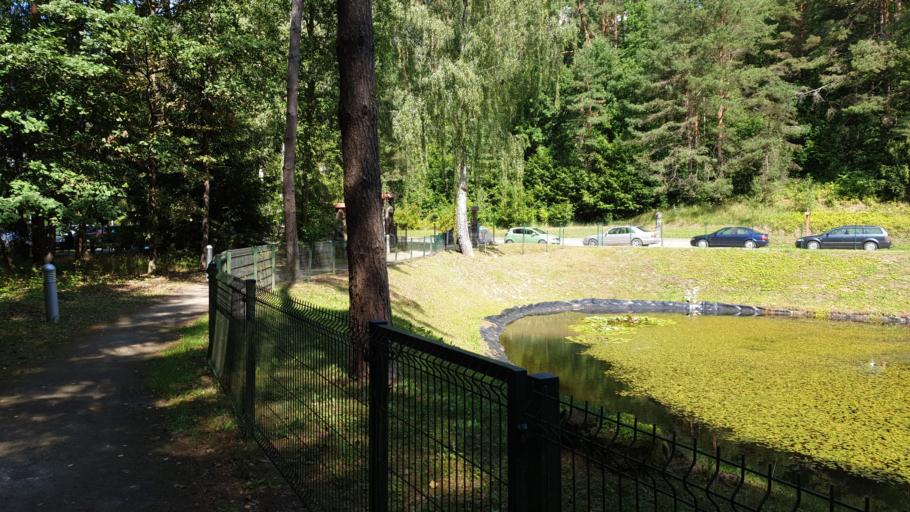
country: LT
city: Birstonas
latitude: 54.6046
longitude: 23.9986
